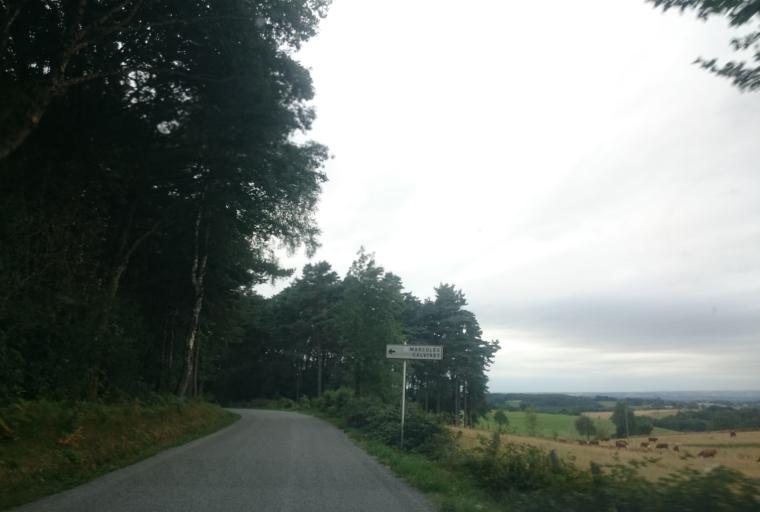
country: FR
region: Auvergne
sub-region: Departement du Cantal
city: Sansac-de-Marmiesse
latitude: 44.8133
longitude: 2.3739
